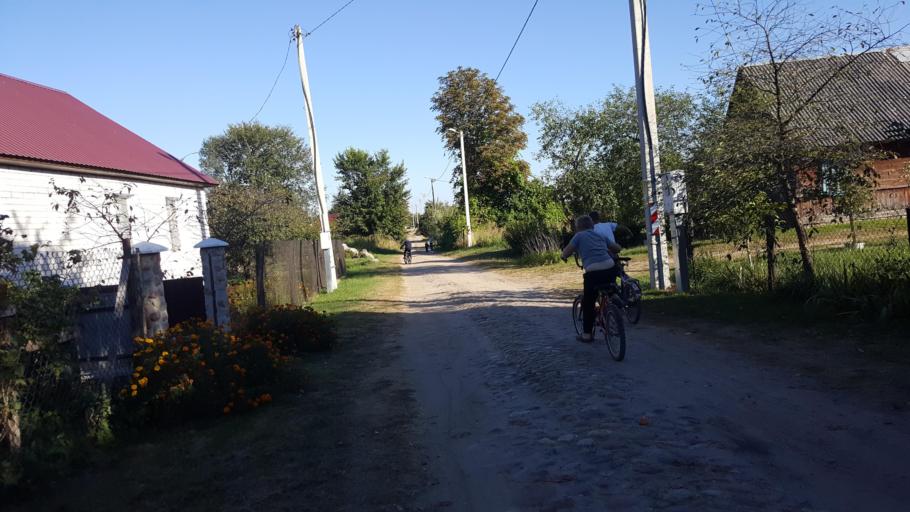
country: BY
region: Brest
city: Vysokaye
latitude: 52.3269
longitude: 23.2676
